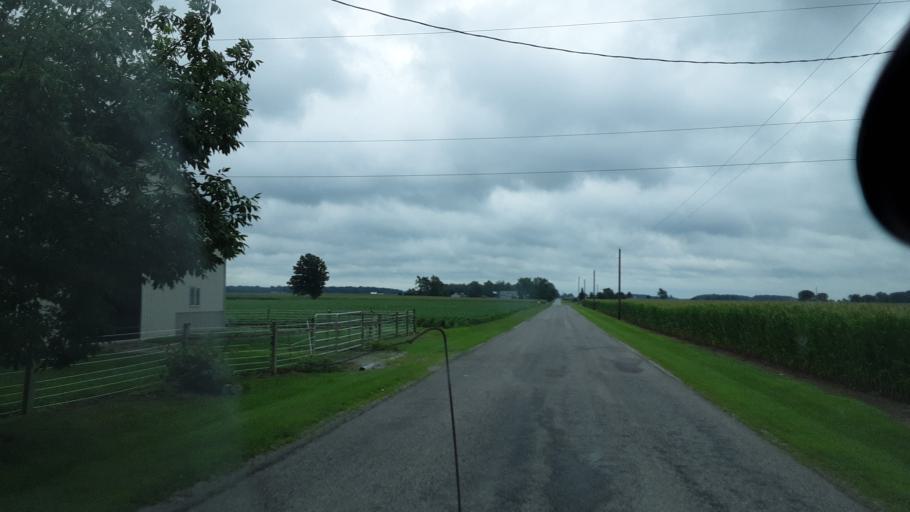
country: US
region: Indiana
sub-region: Wells County
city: Ossian
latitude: 40.9204
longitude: -85.1098
